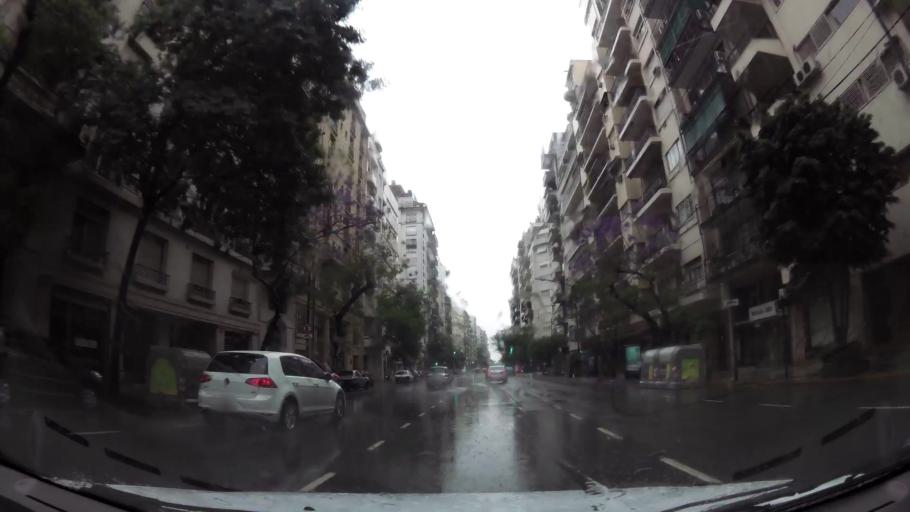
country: AR
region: Buenos Aires F.D.
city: Retiro
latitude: -34.5898
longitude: -58.3896
